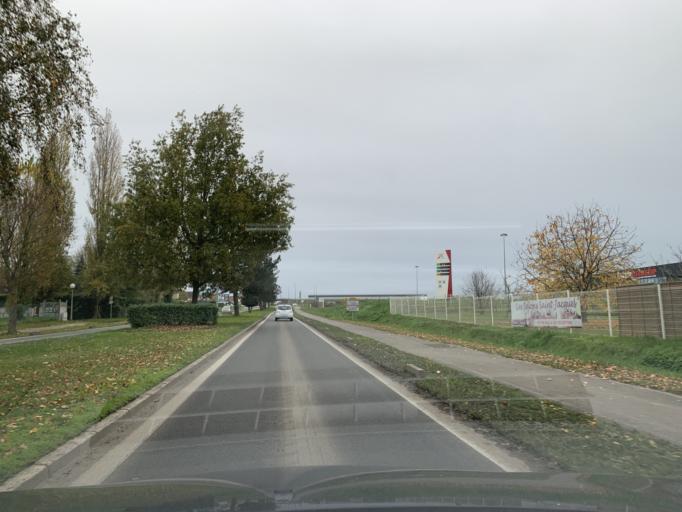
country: FR
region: Nord-Pas-de-Calais
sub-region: Departement du Nord
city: Neuville-Saint-Remy
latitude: 50.1929
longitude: 3.2124
